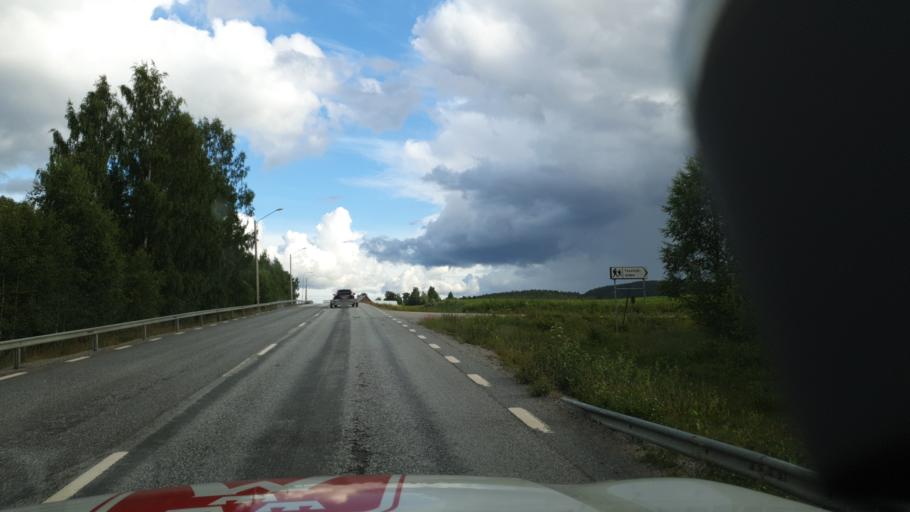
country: SE
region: Vaesterbotten
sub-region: Vannas Kommun
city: Vannasby
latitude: 64.0208
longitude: 20.0262
